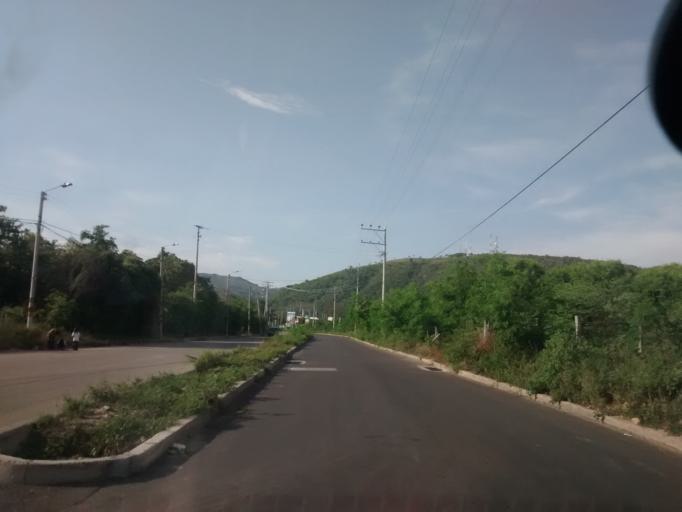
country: CO
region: Cundinamarca
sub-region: Girardot
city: Girardot City
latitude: 4.3113
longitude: -74.8158
